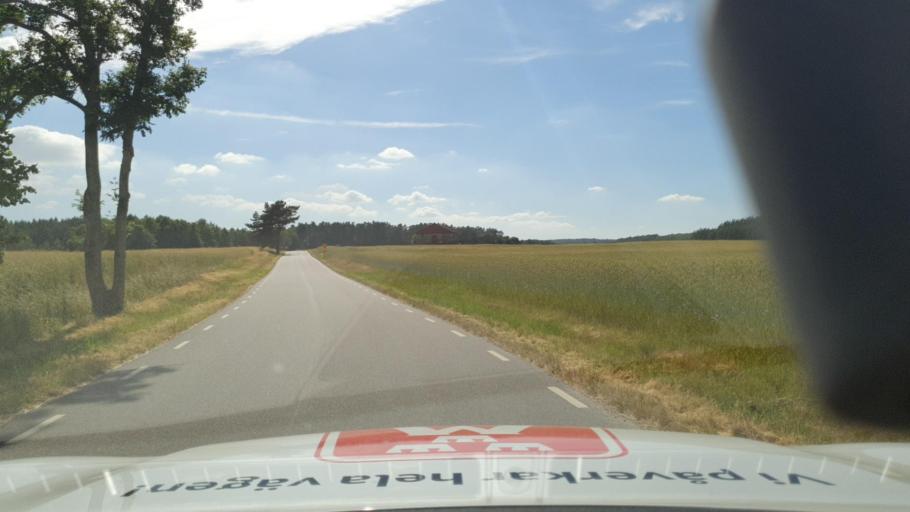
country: SE
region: Skane
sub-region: Sjobo Kommun
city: Blentarp
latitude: 55.6071
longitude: 13.5858
